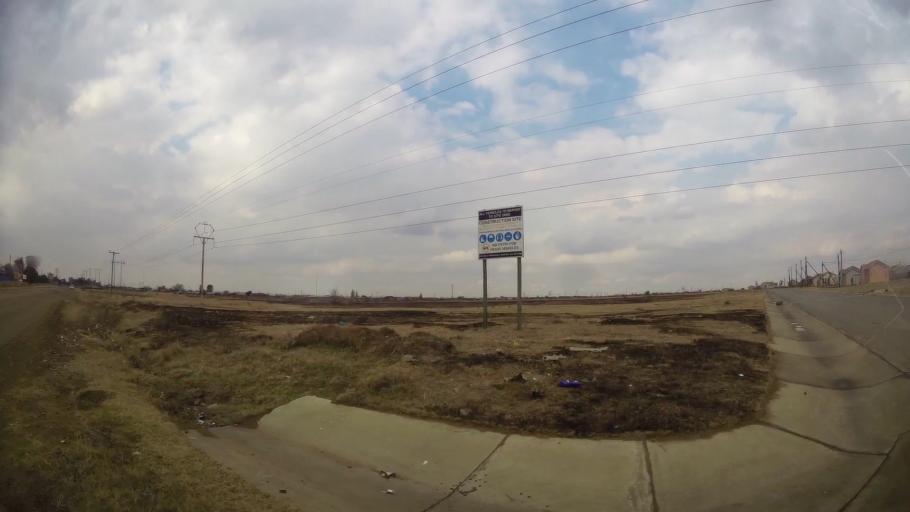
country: ZA
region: Orange Free State
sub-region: Fezile Dabi District Municipality
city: Sasolburg
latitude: -26.8566
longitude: 27.8659
